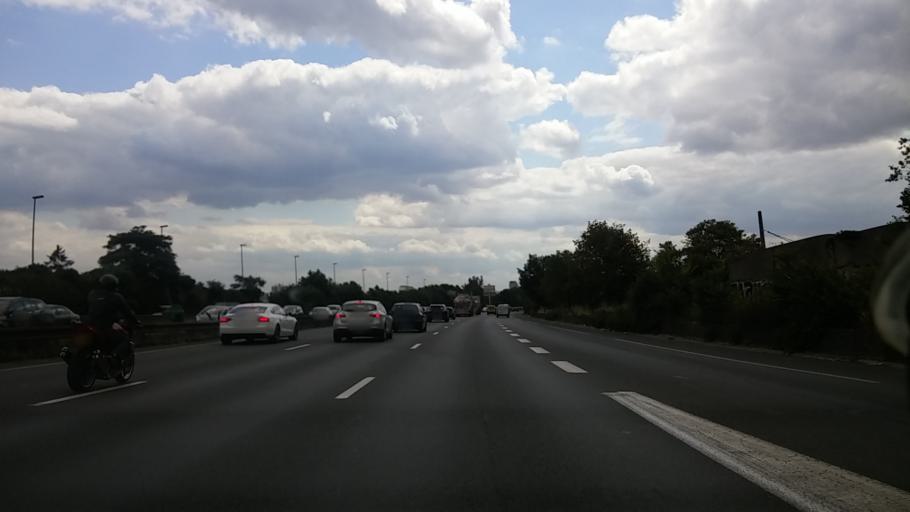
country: FR
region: Ile-de-France
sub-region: Departement de Seine-Saint-Denis
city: Aulnay-sous-Bois
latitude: 48.9266
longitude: 2.4813
